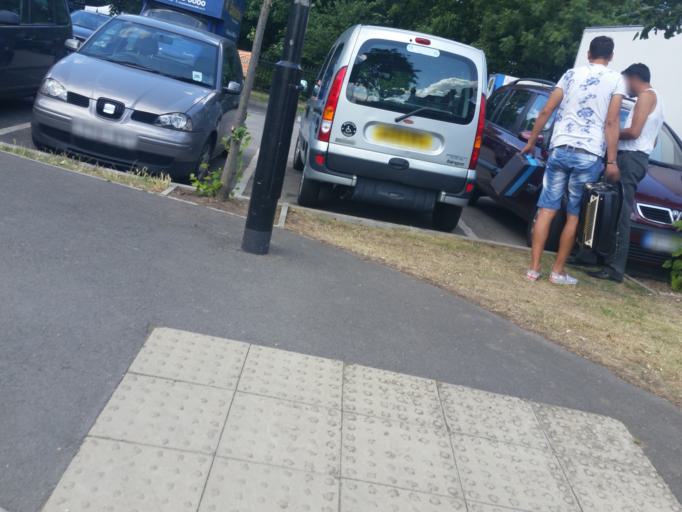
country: GB
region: England
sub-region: Greater London
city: Crouch End
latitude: 51.5880
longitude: -0.1333
